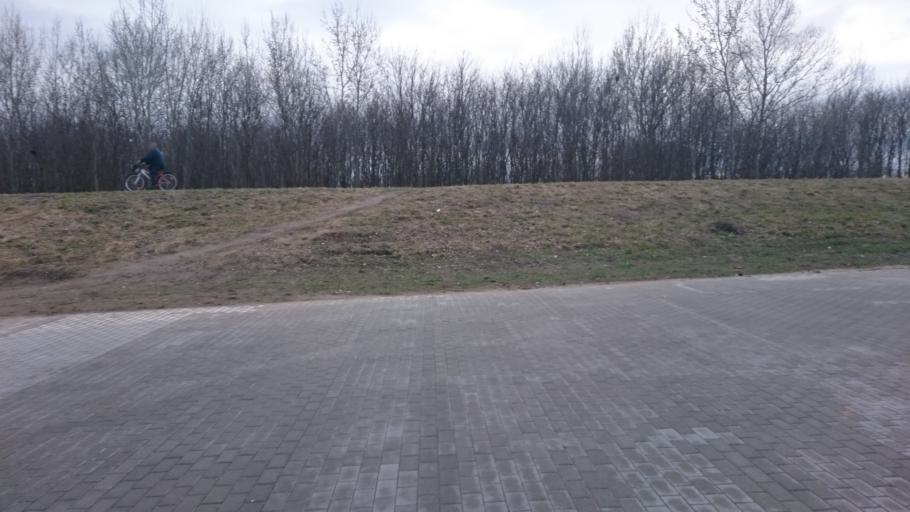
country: SK
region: Nitriansky
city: Sellye
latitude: 48.1617
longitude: 17.8844
